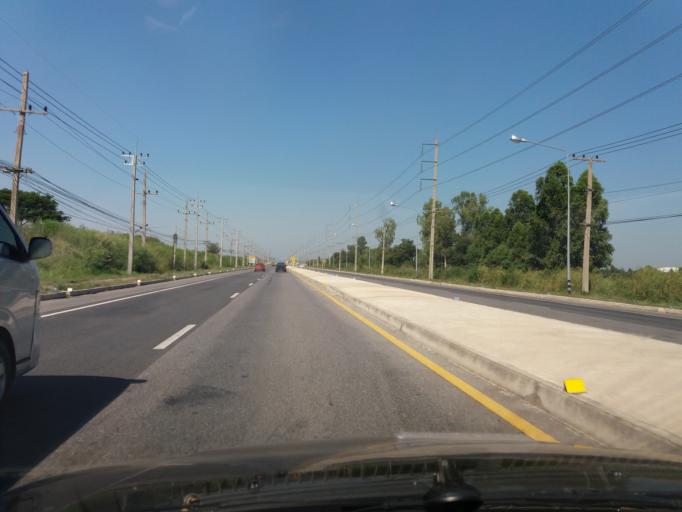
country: TH
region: Chai Nat
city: Manorom
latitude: 15.2924
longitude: 100.0985
